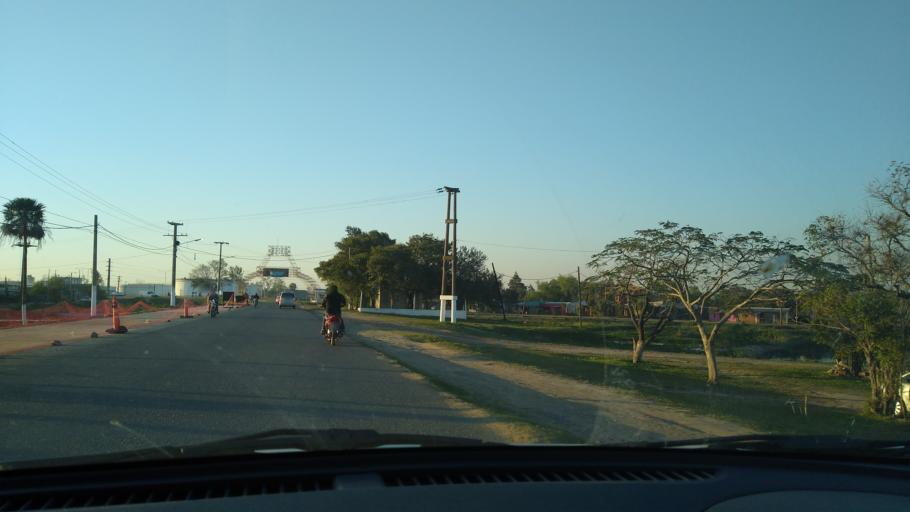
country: AR
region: Chaco
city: Puerto Vilelas
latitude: -27.5050
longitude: -58.9424
